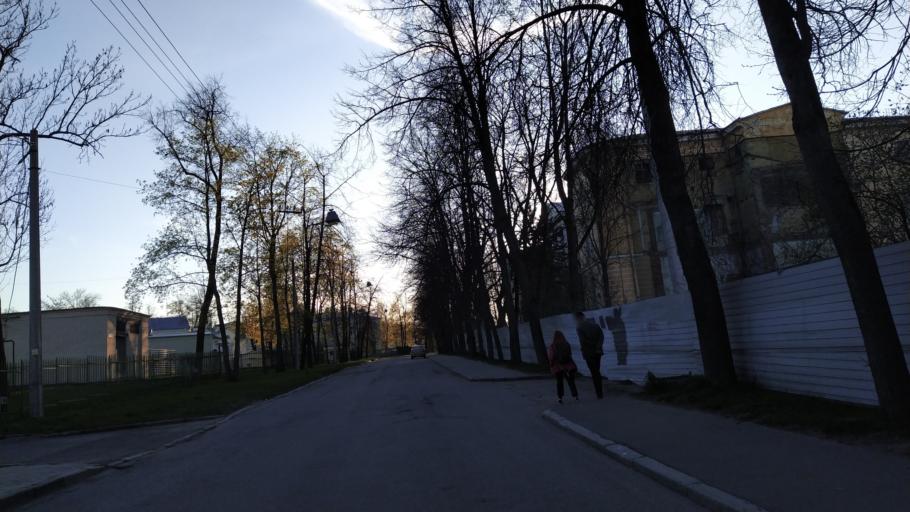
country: RU
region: St.-Petersburg
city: Pushkin
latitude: 59.7137
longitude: 30.4164
